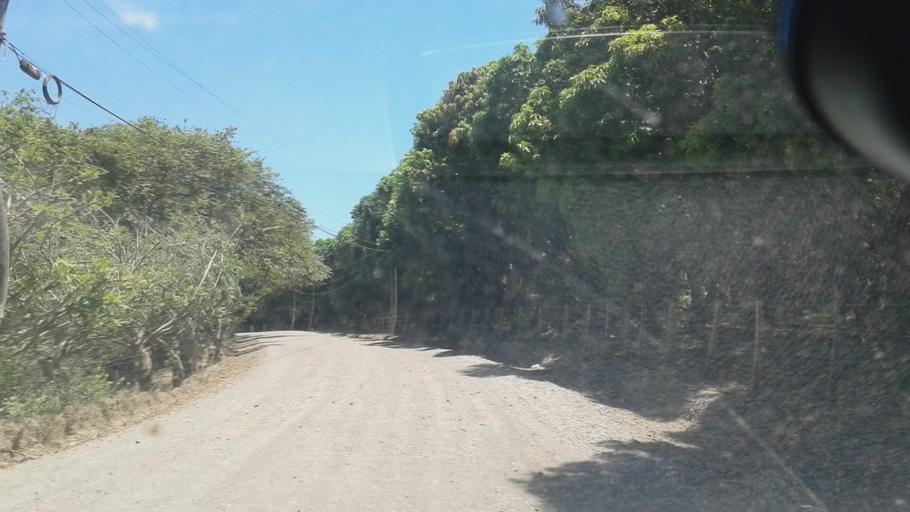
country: CR
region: Guanacaste
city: Samara
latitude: 9.9931
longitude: -85.6746
